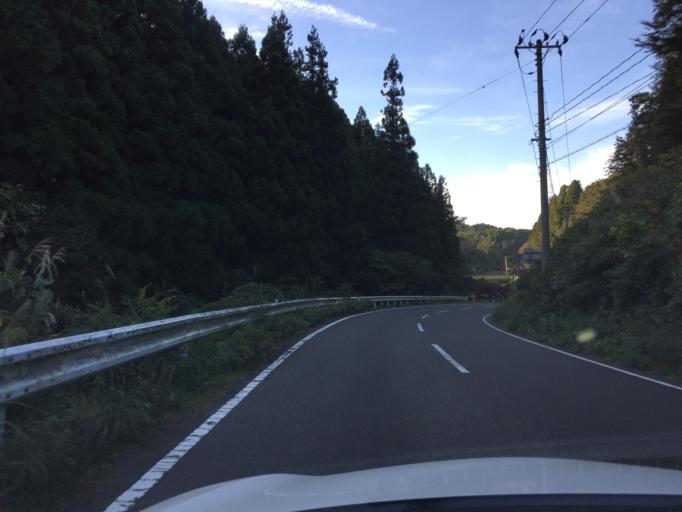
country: JP
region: Fukushima
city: Ishikawa
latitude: 37.2044
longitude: 140.5861
